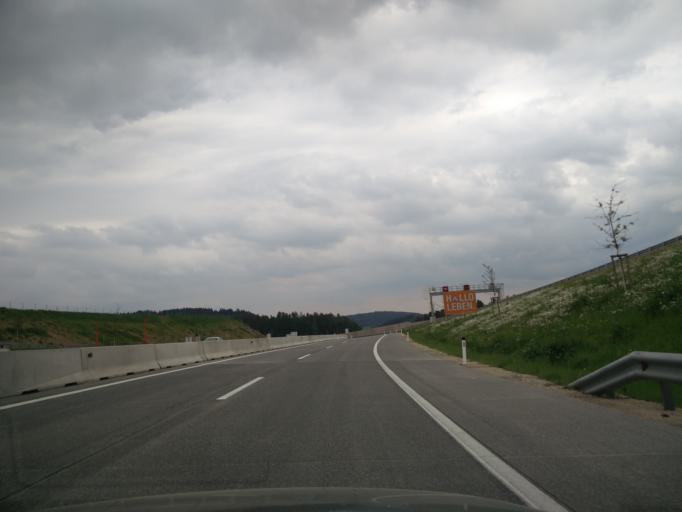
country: AT
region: Upper Austria
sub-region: Politischer Bezirk Urfahr-Umgebung
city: Alberndorf in der Riedmark
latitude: 48.4181
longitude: 14.4889
